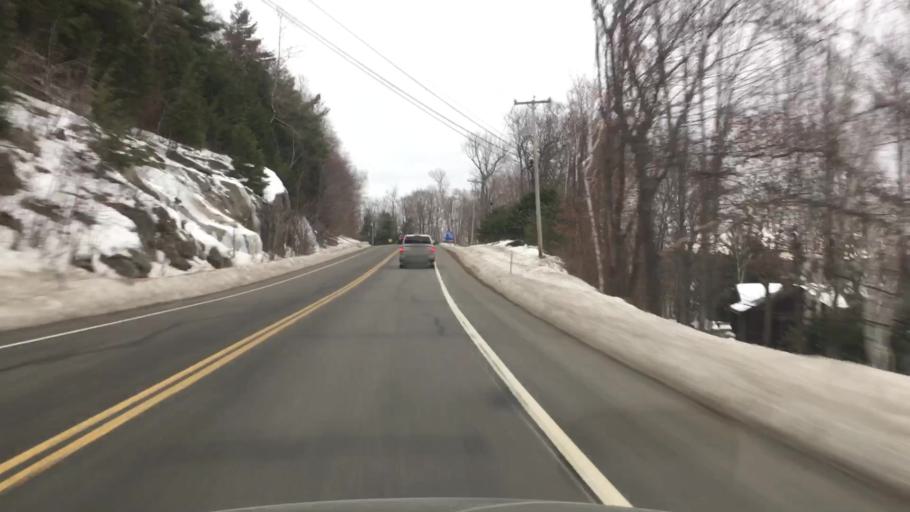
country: US
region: New Hampshire
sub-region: Merrimack County
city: Newbury
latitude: 43.3375
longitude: -72.0557
